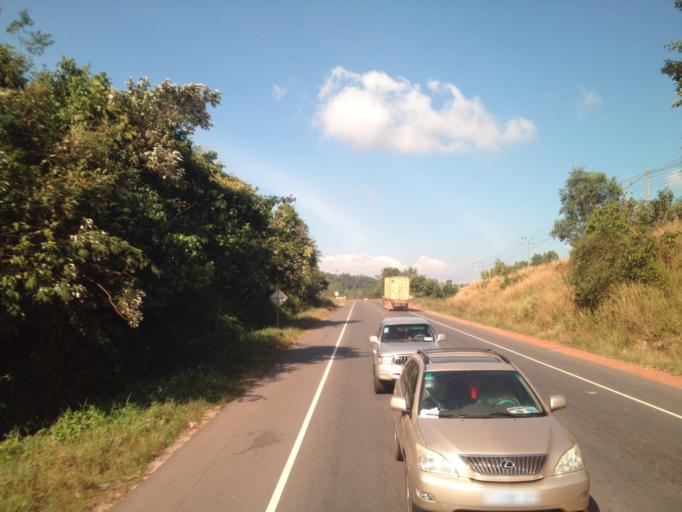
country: KH
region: Preah Sihanouk
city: Sihanoukville
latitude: 10.6059
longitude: 103.6182
